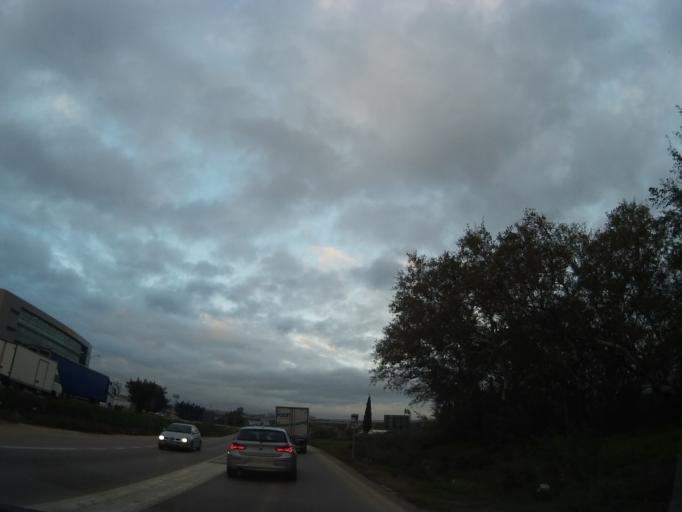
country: ES
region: Andalusia
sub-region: Provincia de Malaga
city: Alhaurin de la Torre
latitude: 36.7065
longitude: -4.5102
